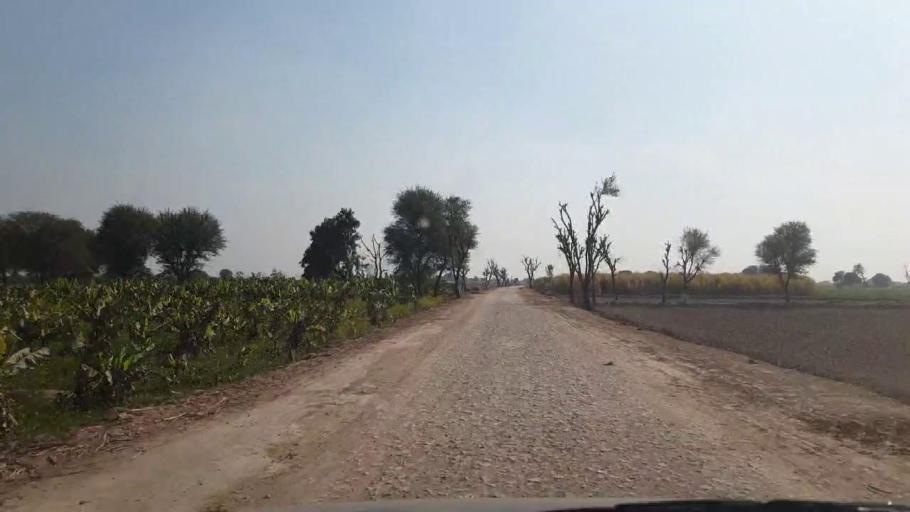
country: PK
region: Sindh
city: Chambar
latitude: 25.3419
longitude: 68.7712
